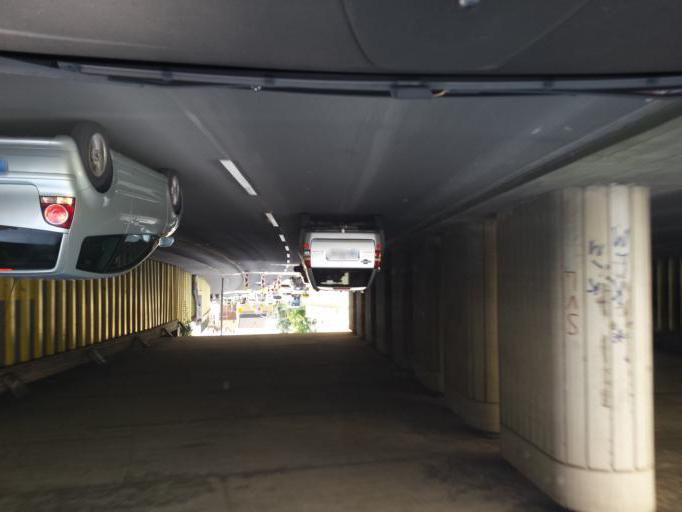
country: DE
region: North Rhine-Westphalia
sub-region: Regierungsbezirk Arnsberg
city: Lippstadt
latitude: 51.6702
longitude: 8.3377
